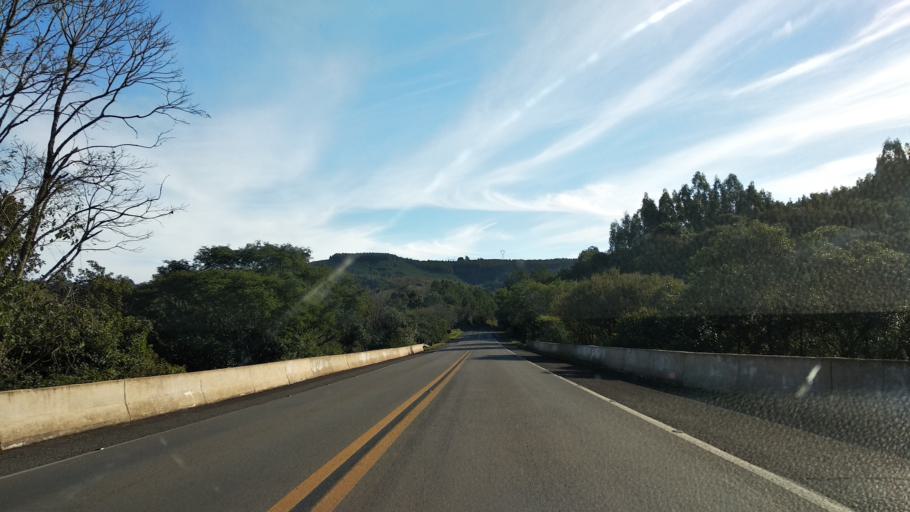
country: BR
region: Santa Catarina
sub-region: Celso Ramos
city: Celso Ramos
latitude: -27.5495
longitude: -51.4417
